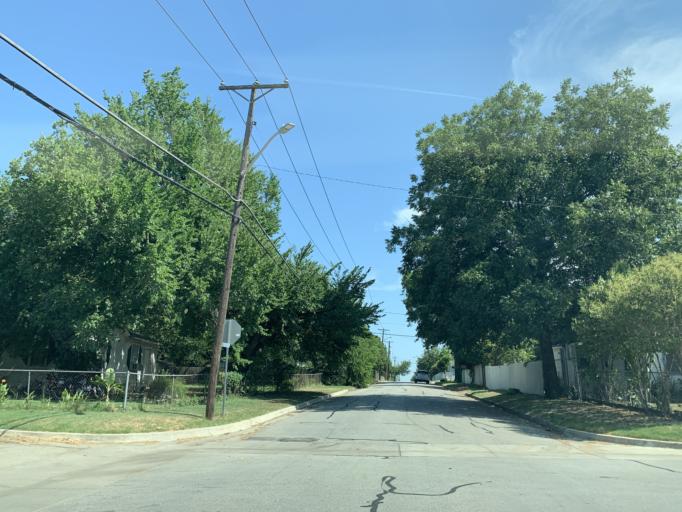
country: US
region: Texas
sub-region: Tarrant County
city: Fort Worth
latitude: 32.6953
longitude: -97.3185
